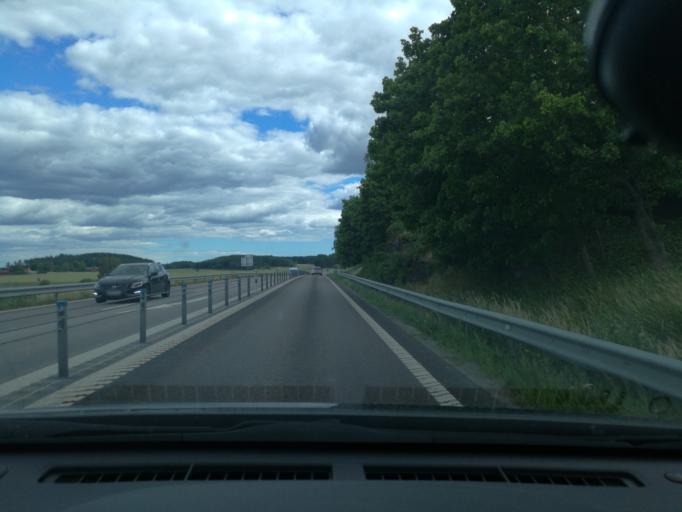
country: SE
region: OEstergoetland
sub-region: Soderkopings Kommun
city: Soederkoeping
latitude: 58.5404
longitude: 16.2748
